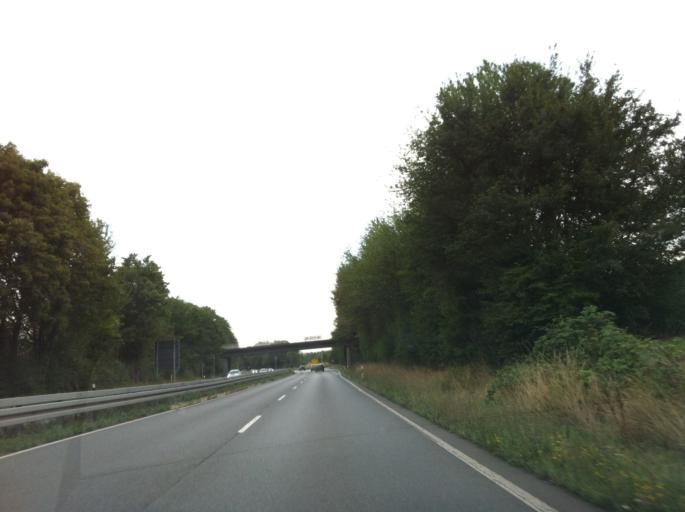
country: DE
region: Hesse
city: Schwalbach am Taunus
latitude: 50.1466
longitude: 8.5504
